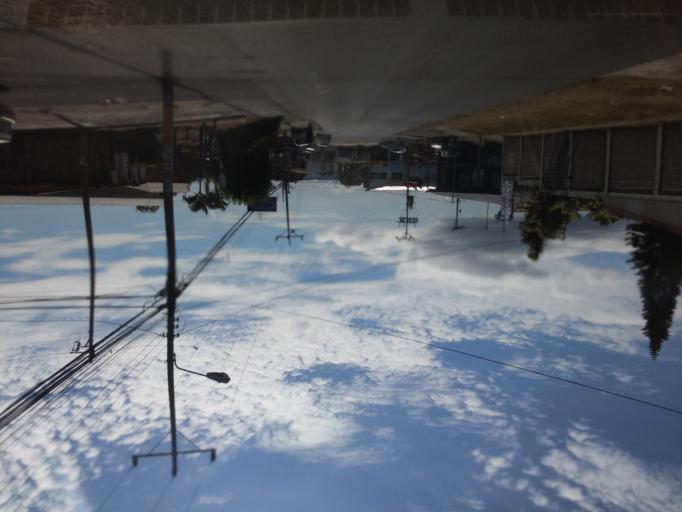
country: CR
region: Alajuela
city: Alajuela
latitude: 10.0224
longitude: -84.1891
